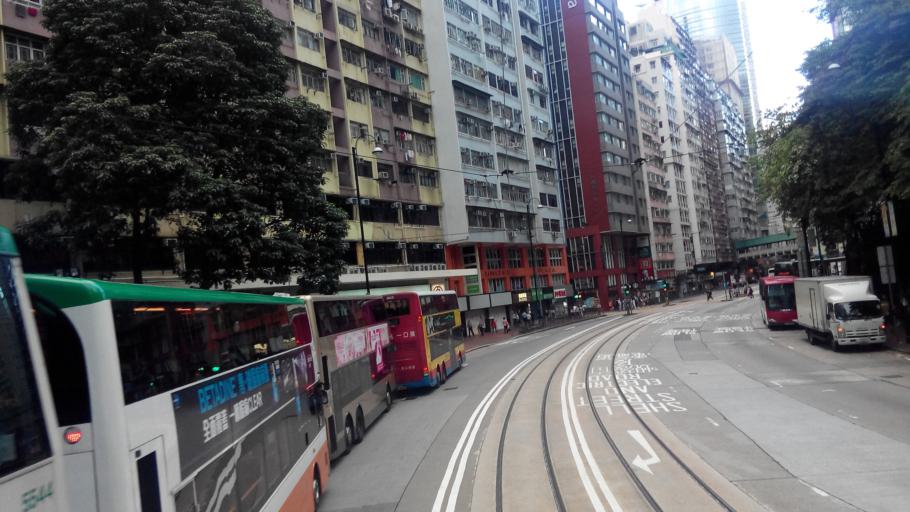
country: HK
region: Wanchai
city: Wan Chai
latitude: 22.2874
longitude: 114.1930
